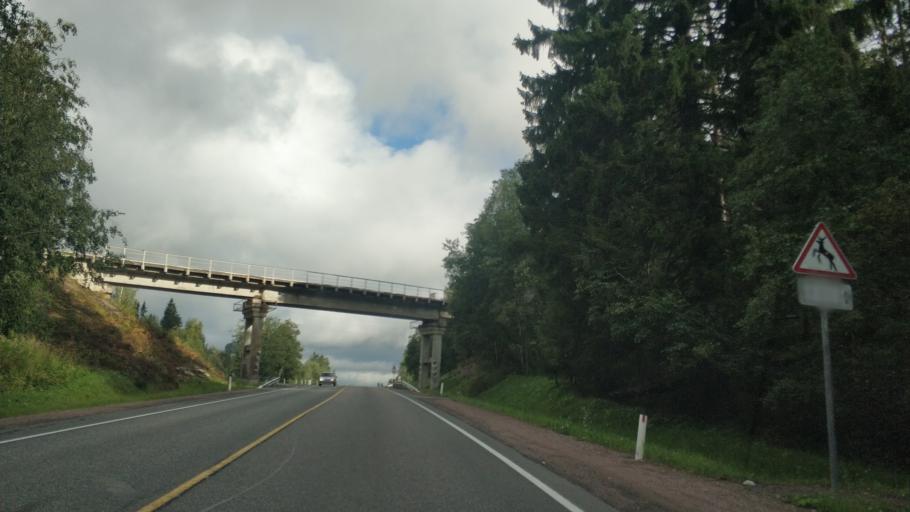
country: RU
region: Republic of Karelia
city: Khelyulya
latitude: 61.7778
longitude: 30.6606
